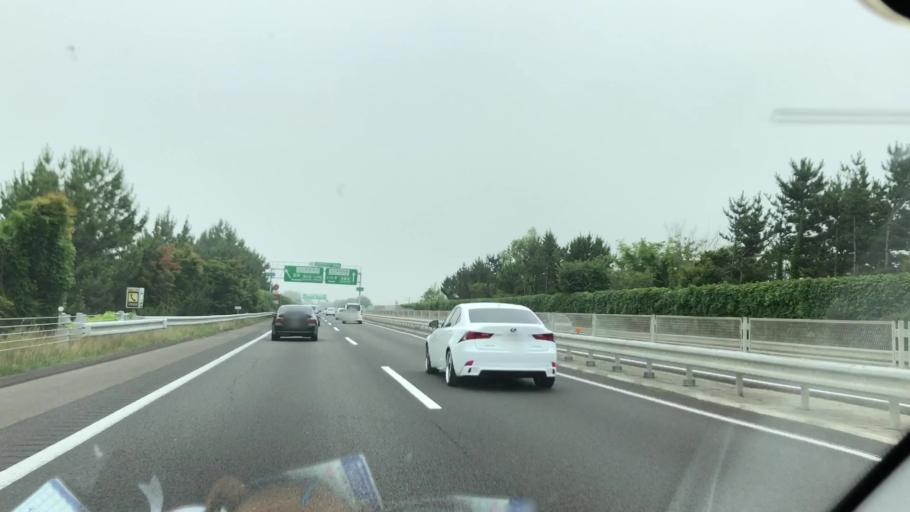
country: JP
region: Miyagi
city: Sendai
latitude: 38.2158
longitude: 140.9481
